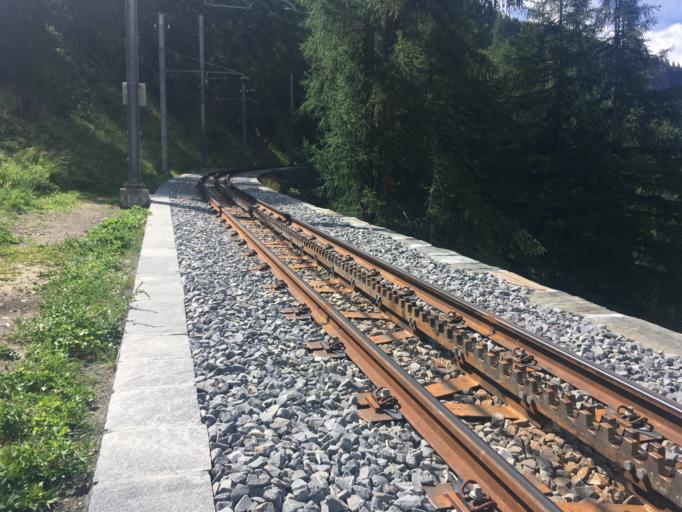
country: CH
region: Valais
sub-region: Visp District
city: Zermatt
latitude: 46.0150
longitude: 7.7498
